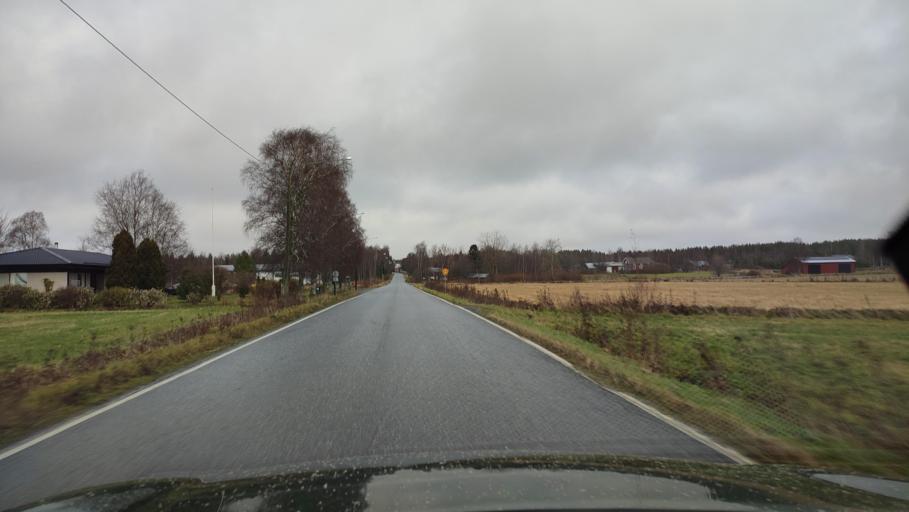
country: FI
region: Ostrobothnia
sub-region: Sydosterbotten
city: Kristinestad
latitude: 62.3109
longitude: 21.4828
